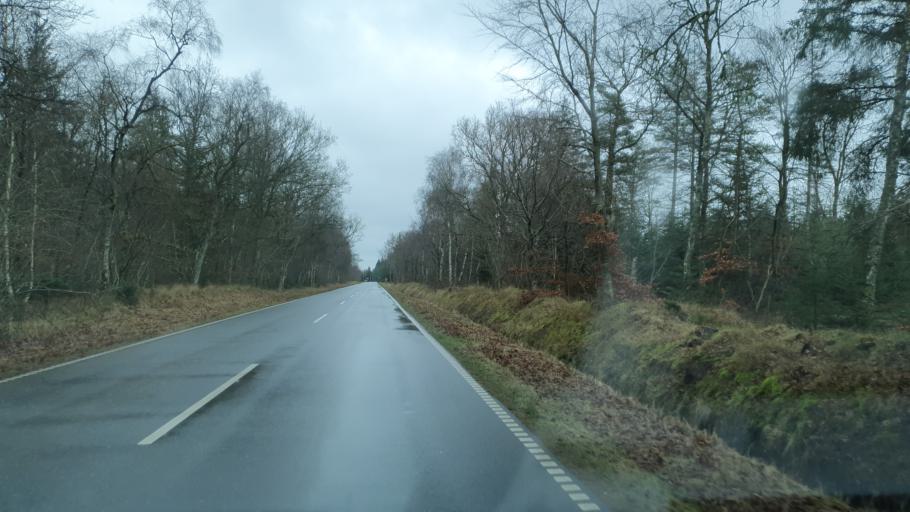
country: DK
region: North Denmark
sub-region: Jammerbugt Kommune
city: Fjerritslev
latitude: 57.1258
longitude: 9.1304
